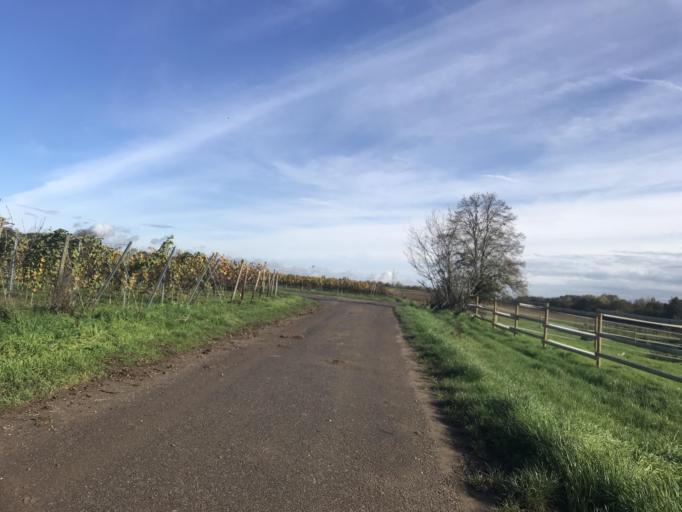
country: DE
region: Hesse
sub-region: Regierungsbezirk Darmstadt
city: Hochheim am Main
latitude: 50.0155
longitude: 8.3187
